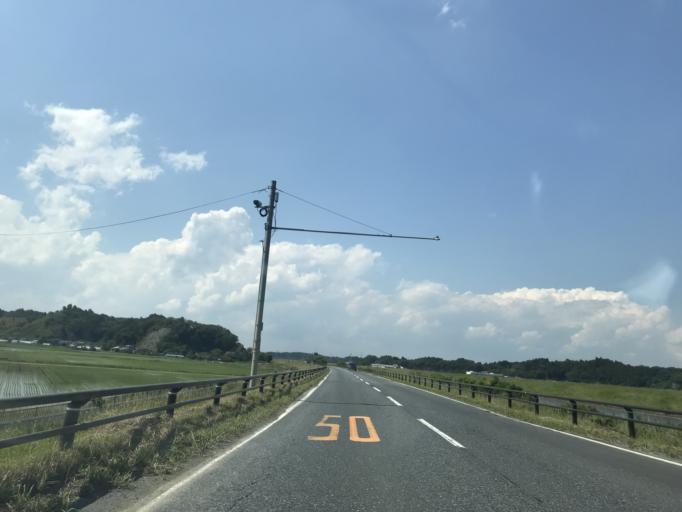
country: JP
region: Miyagi
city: Yamoto
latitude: 38.3973
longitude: 141.1552
